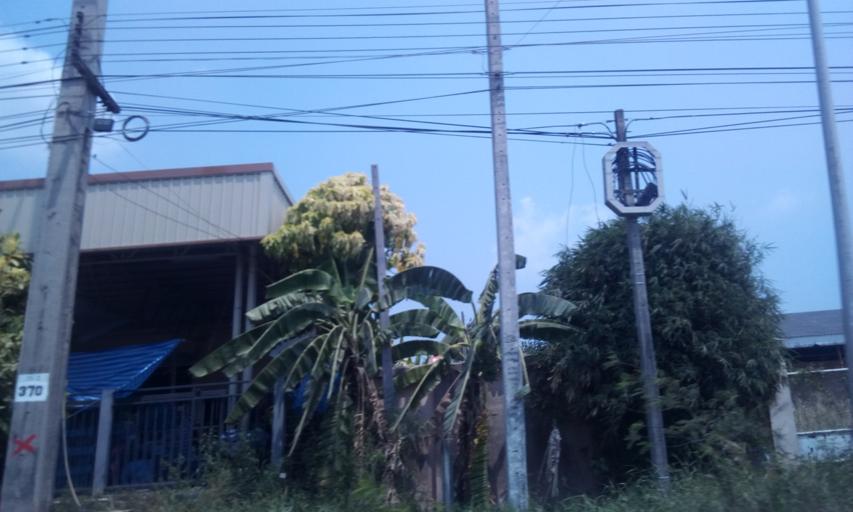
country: TH
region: Chachoengsao
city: Ban Pho
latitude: 13.6042
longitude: 101.1162
